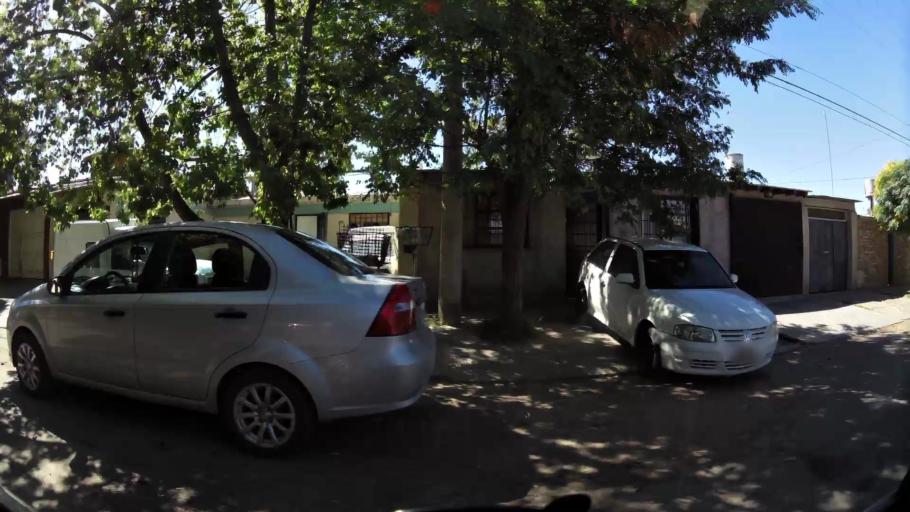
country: AR
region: Mendoza
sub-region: Departamento de Godoy Cruz
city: Godoy Cruz
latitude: -32.9667
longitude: -68.8360
